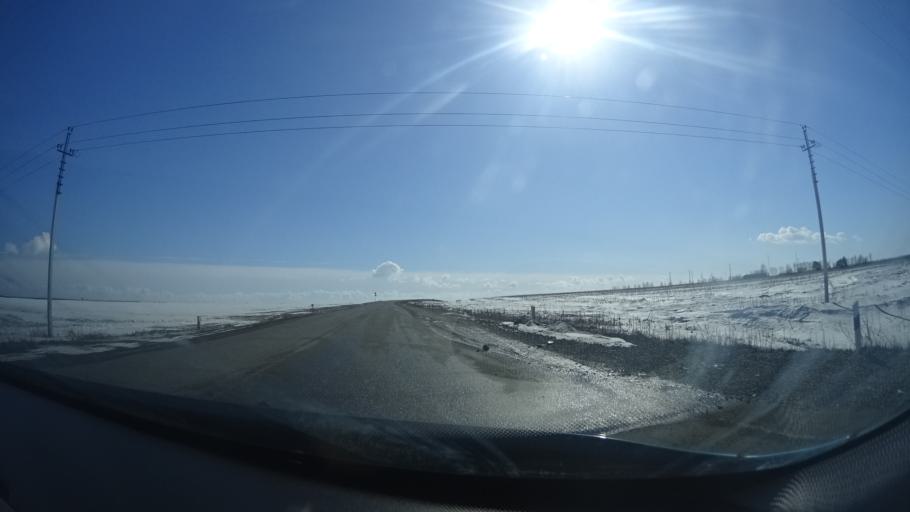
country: RU
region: Bashkortostan
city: Avdon
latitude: 54.6042
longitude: 55.8479
